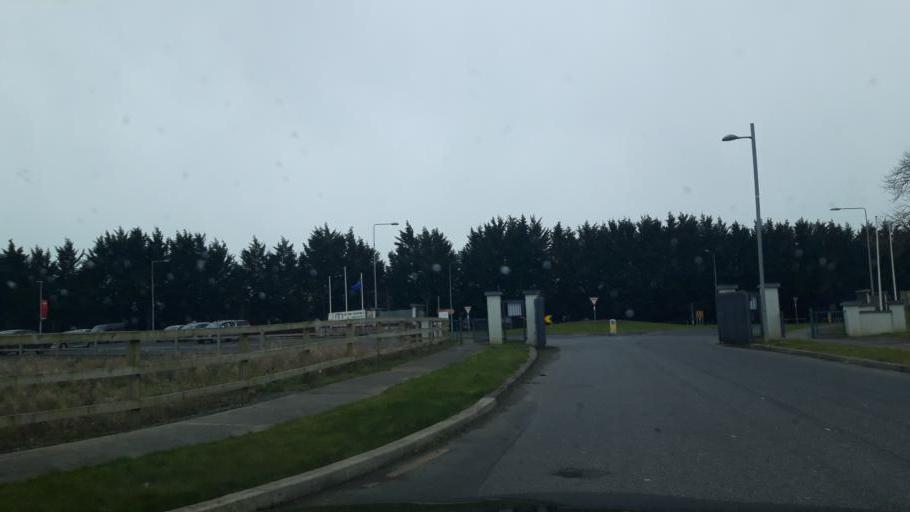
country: IE
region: Leinster
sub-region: Kilkenny
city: Kilkenny
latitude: 52.6492
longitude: -7.2124
